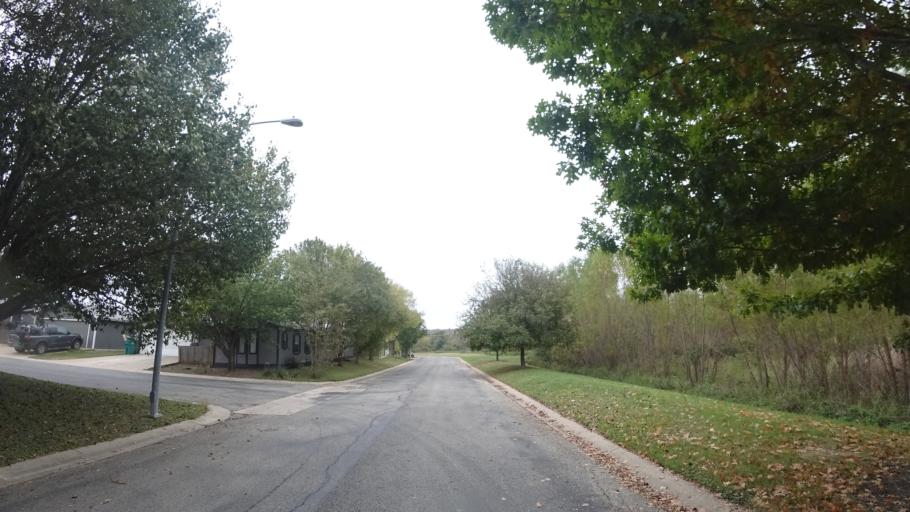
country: US
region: Texas
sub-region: Travis County
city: Pflugerville
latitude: 30.3882
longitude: -97.6419
